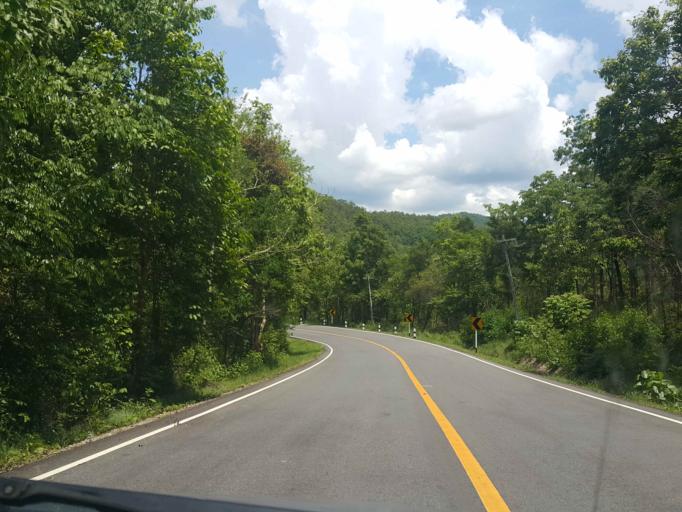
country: TH
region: Phayao
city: Chiang Muan
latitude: 18.8489
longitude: 100.3249
